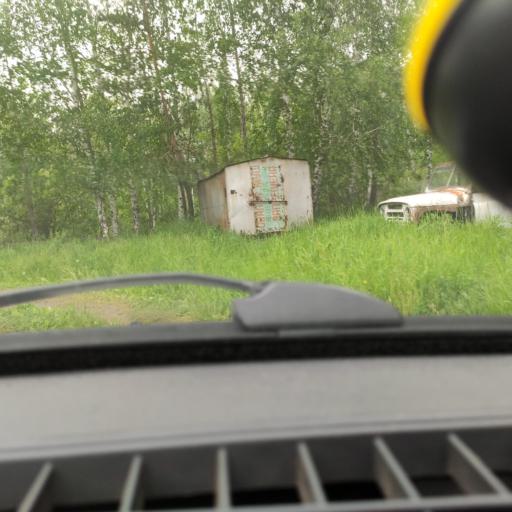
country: RU
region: Samara
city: Zhigulevsk
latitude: 53.5043
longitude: 49.5020
